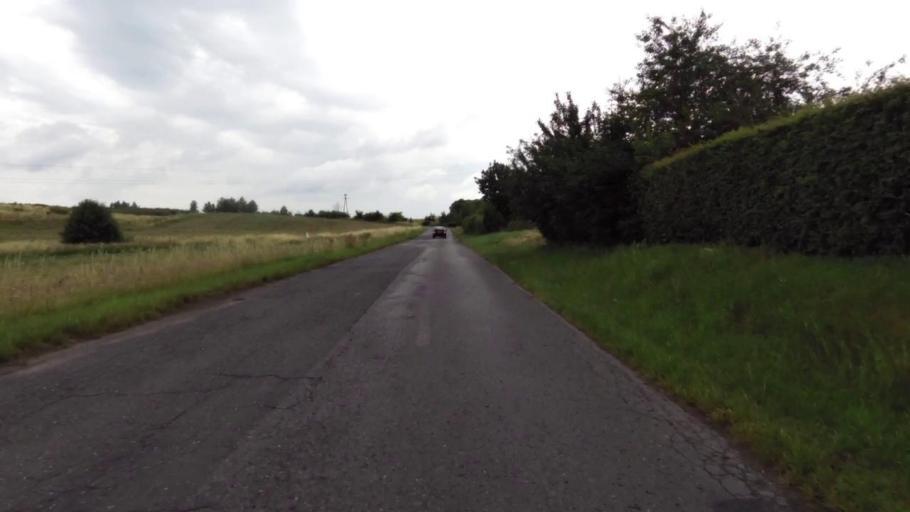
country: PL
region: West Pomeranian Voivodeship
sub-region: Powiat mysliborski
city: Mysliborz
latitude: 52.9356
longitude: 14.8757
